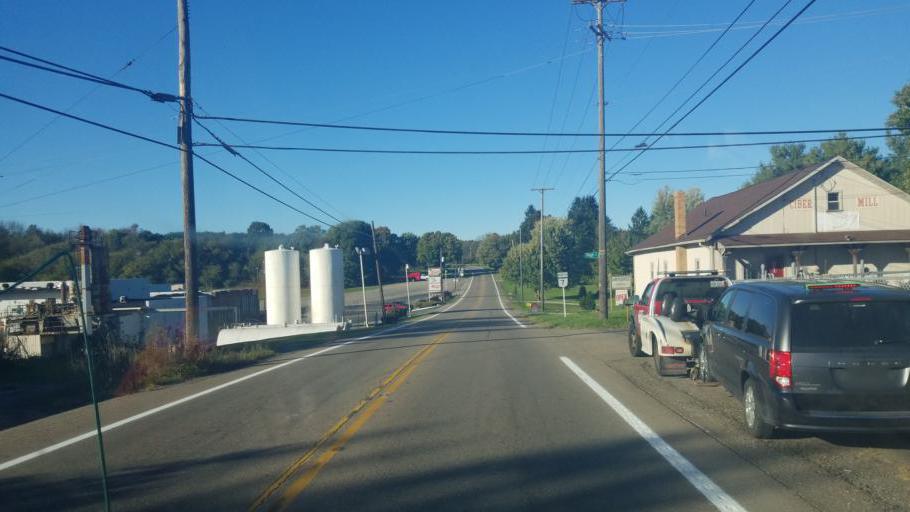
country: US
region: Ohio
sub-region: Columbiana County
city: New Waterford
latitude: 40.8221
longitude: -80.6363
